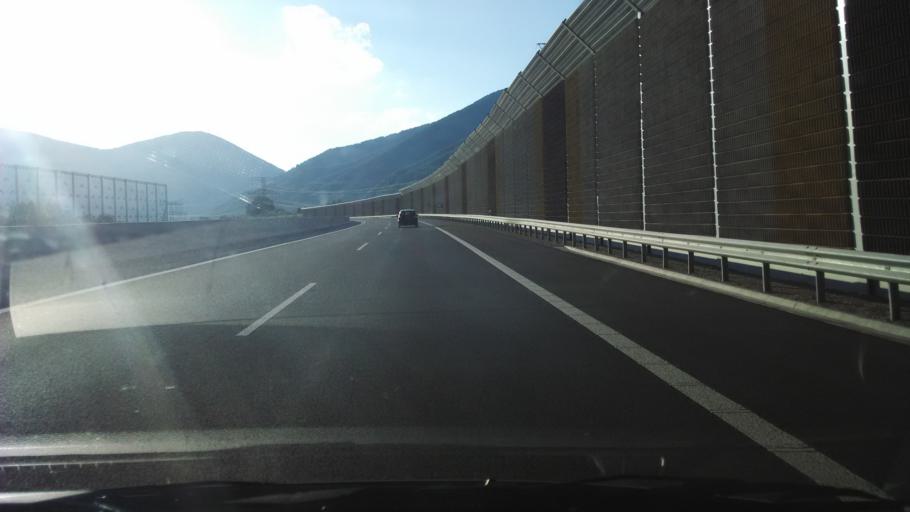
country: SK
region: Zilinsky
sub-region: Okres Zilina
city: Vrutky
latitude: 49.1181
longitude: 18.9399
